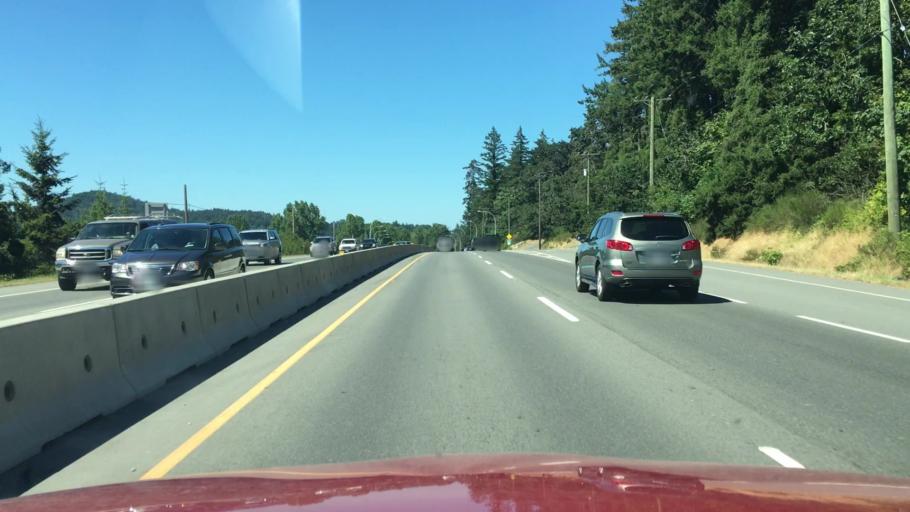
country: CA
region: British Columbia
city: Victoria
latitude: 48.5207
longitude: -123.3857
